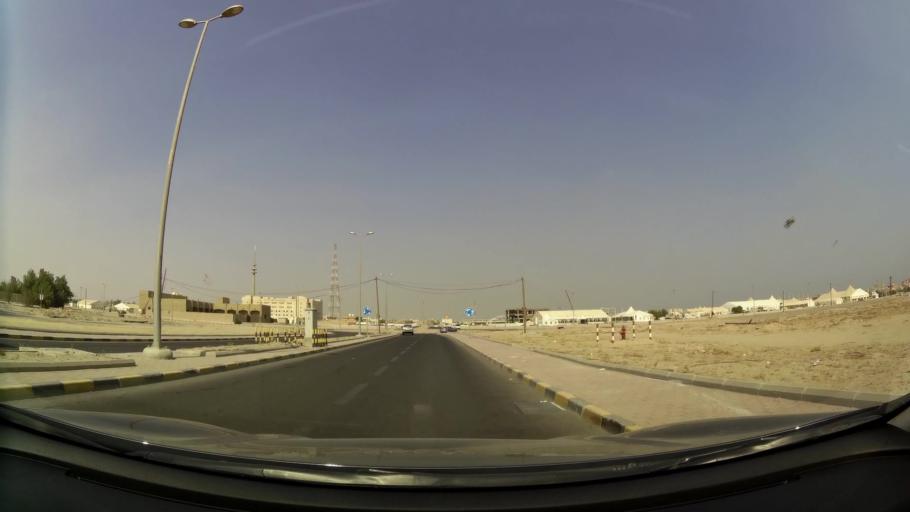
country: KW
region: Al Ahmadi
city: Al Fahahil
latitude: 29.0816
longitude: 48.1078
